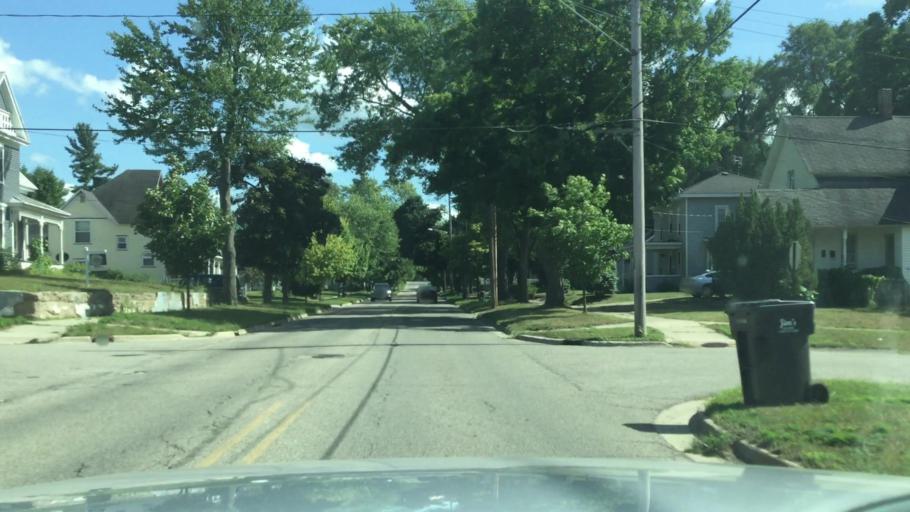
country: US
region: Michigan
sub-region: Ionia County
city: Belding
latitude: 43.0934
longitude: -85.2288
